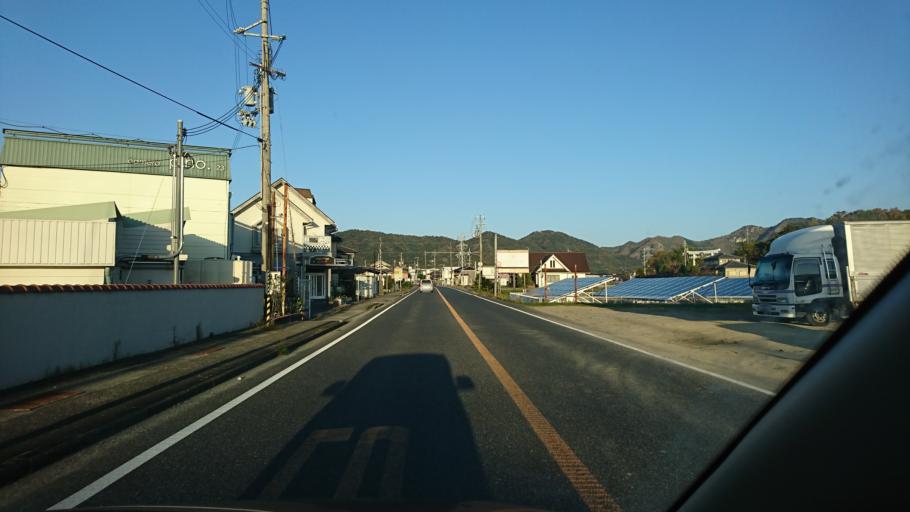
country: JP
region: Hyogo
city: Kakogawacho-honmachi
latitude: 34.7937
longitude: 134.7890
